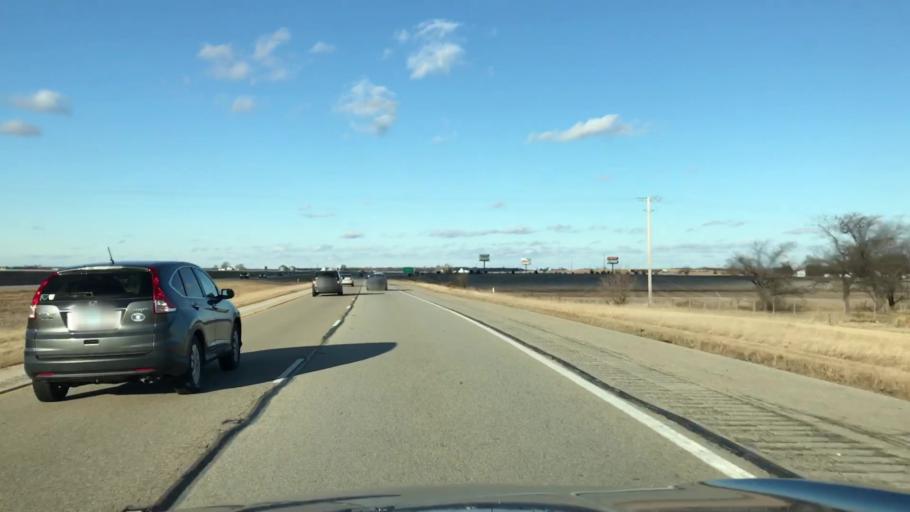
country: US
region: Illinois
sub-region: McLean County
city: Hudson
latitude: 40.5603
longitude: -88.9089
